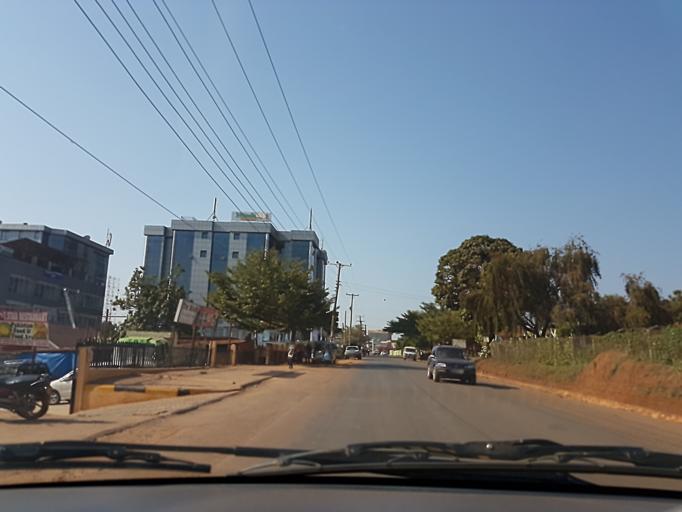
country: UG
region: Central Region
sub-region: Wakiso District
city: Kireka
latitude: 0.3523
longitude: 32.6153
